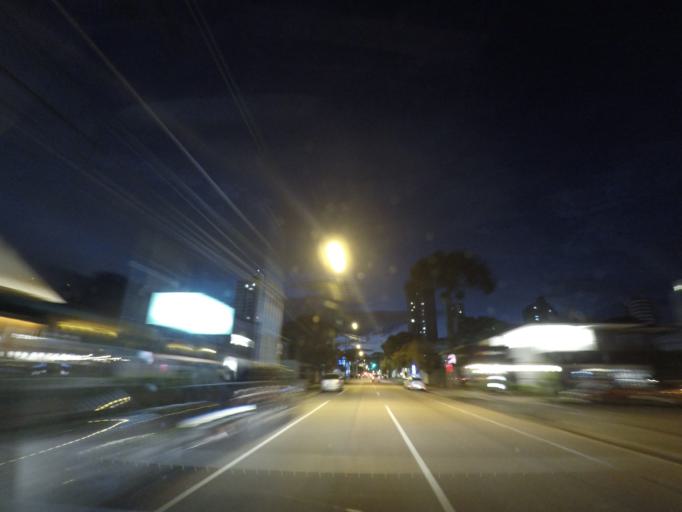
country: BR
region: Parana
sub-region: Curitiba
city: Curitiba
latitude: -25.4154
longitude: -49.2570
